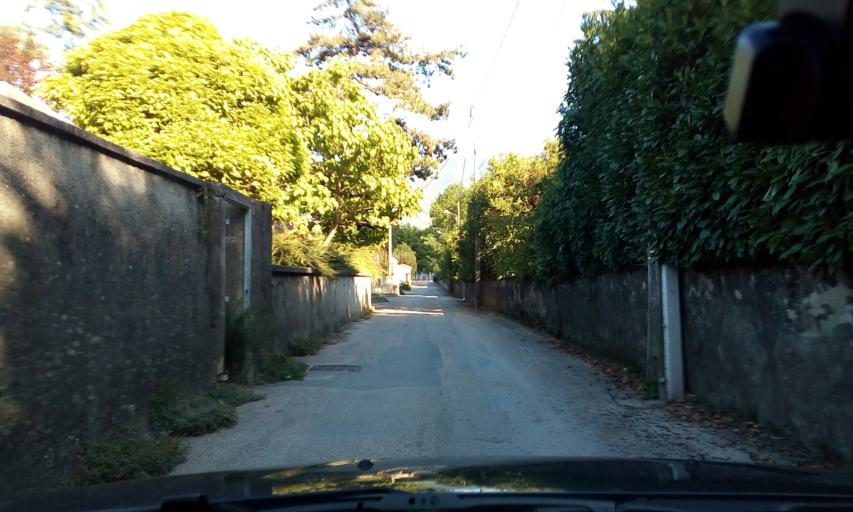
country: FR
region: Rhone-Alpes
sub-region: Departement de l'Isere
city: Vif
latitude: 45.0537
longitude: 5.6703
